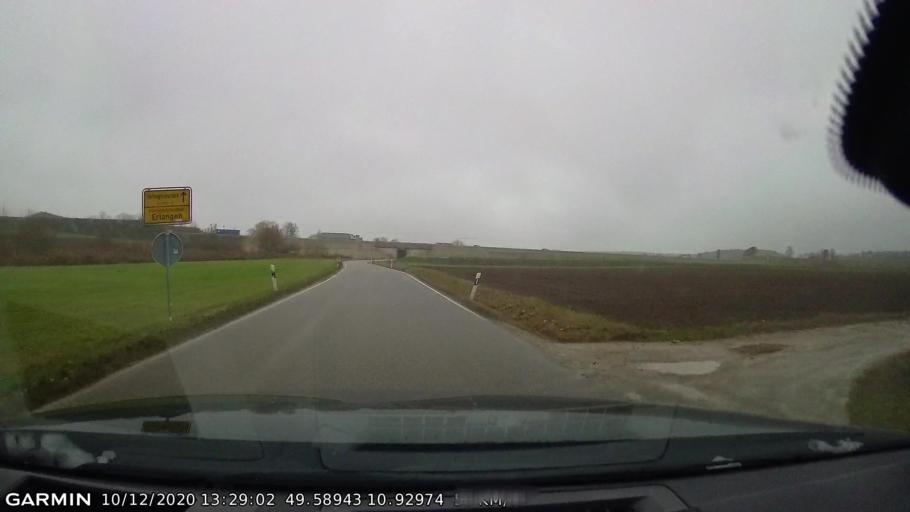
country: DE
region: Bavaria
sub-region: Regierungsbezirk Mittelfranken
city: Hessdorf
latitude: 49.5894
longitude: 10.9296
